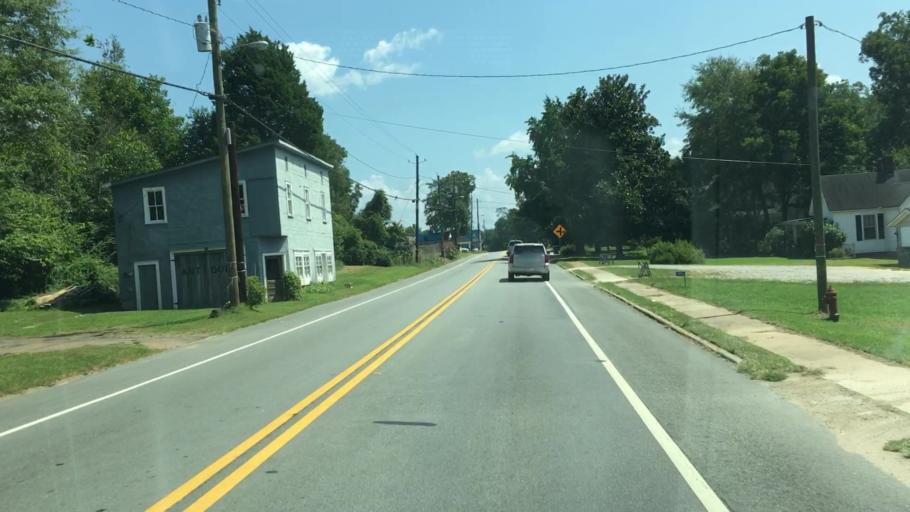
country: US
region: Georgia
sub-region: Oconee County
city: Watkinsville
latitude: 33.8183
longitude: -83.4383
